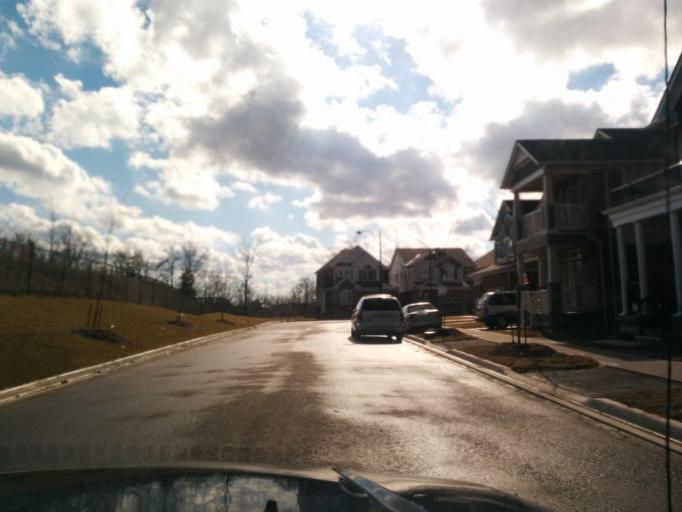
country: CA
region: Ontario
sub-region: Halton
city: Milton
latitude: 43.5022
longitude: -79.8515
